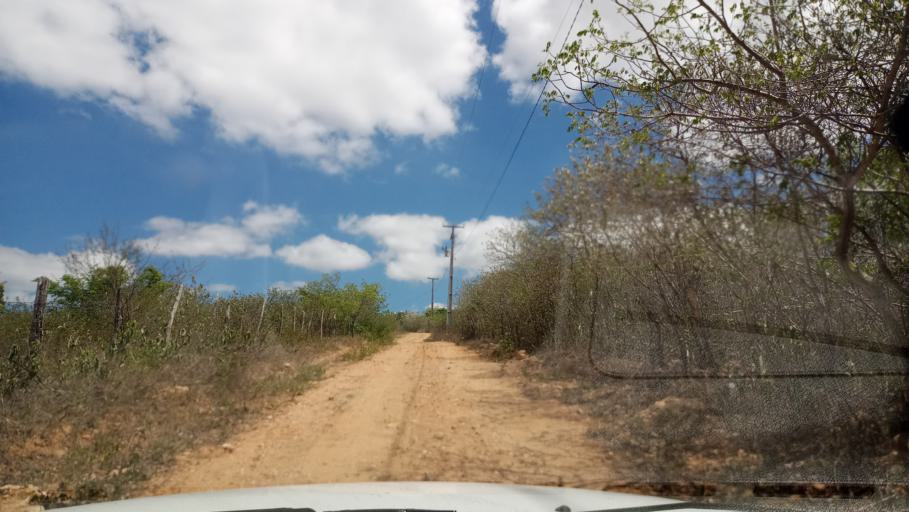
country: BR
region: Rio Grande do Norte
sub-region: Sao Paulo Do Potengi
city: Sao Paulo do Potengi
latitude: -5.7476
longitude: -35.9101
